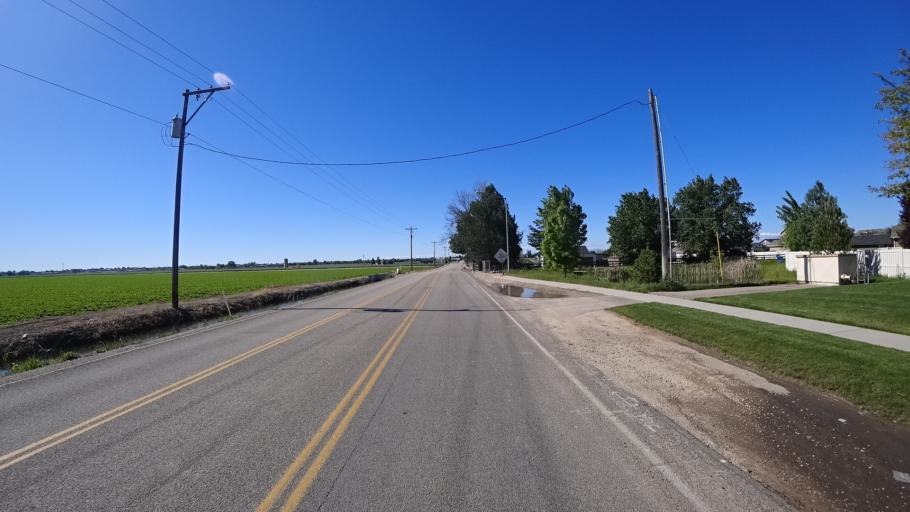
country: US
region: Idaho
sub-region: Ada County
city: Star
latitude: 43.6468
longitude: -116.4537
